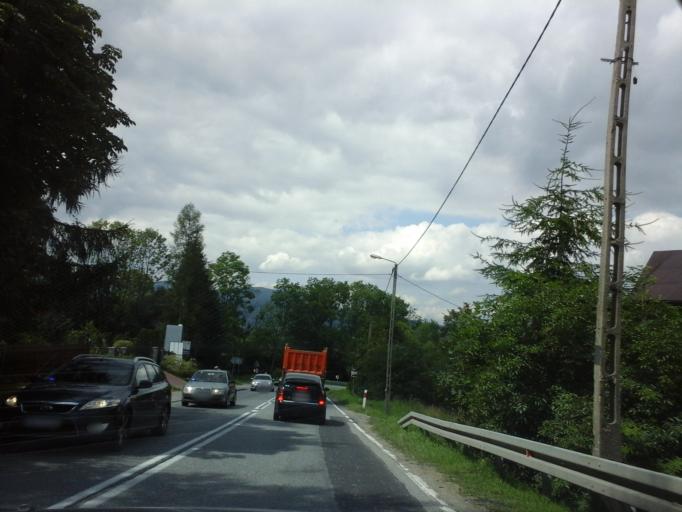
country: PL
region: Lesser Poland Voivodeship
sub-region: Powiat suski
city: Jordanow
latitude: 49.6500
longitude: 19.8275
